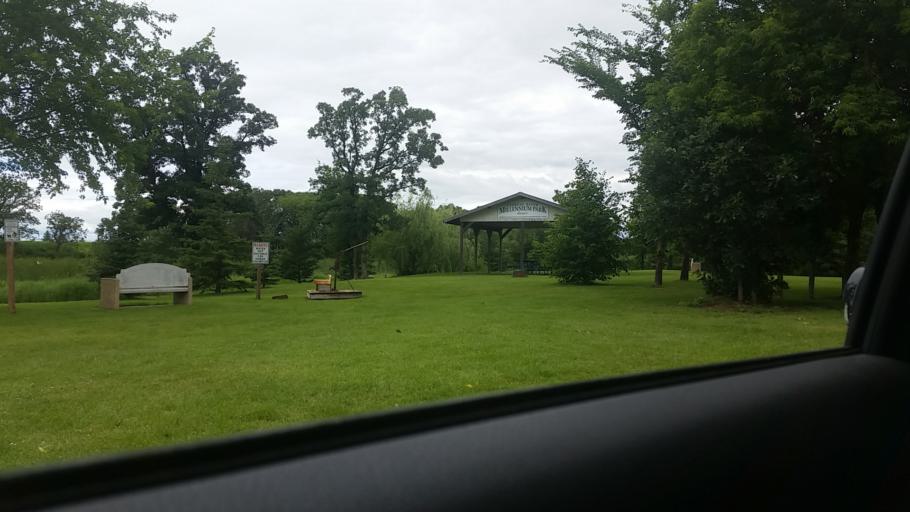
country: CA
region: Manitoba
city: Carberry
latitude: 49.5623
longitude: -99.0842
